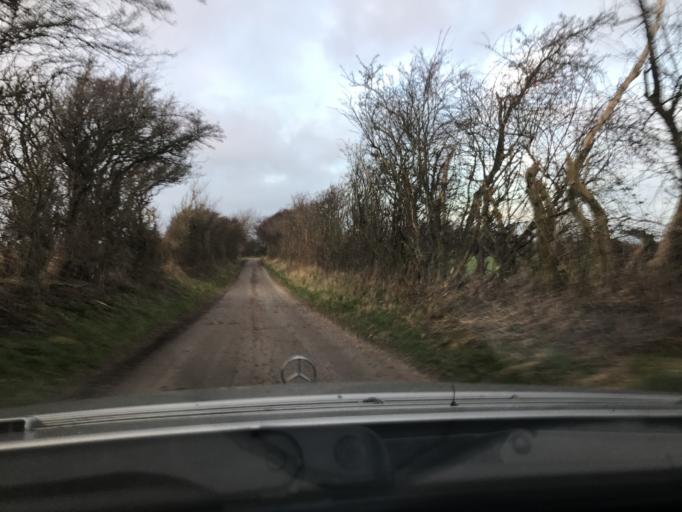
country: DK
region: South Denmark
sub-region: Sonderborg Kommune
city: Nordborg
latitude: 55.0616
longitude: 9.6700
